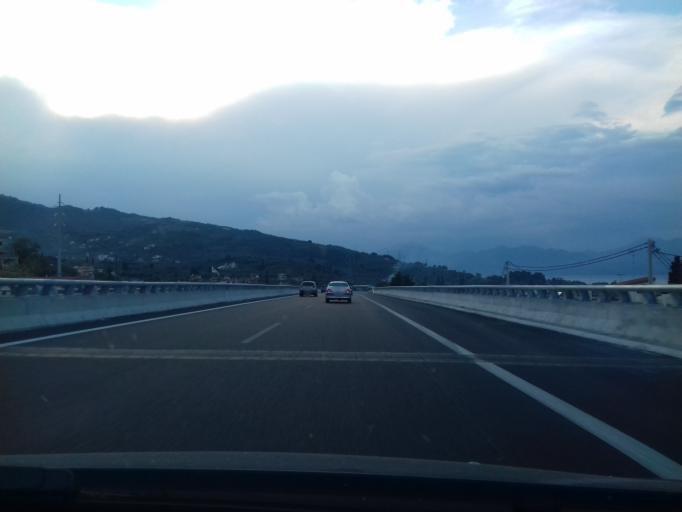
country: GR
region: West Greece
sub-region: Nomos Achaias
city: Kamarai
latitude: 38.2984
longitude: 22.0013
